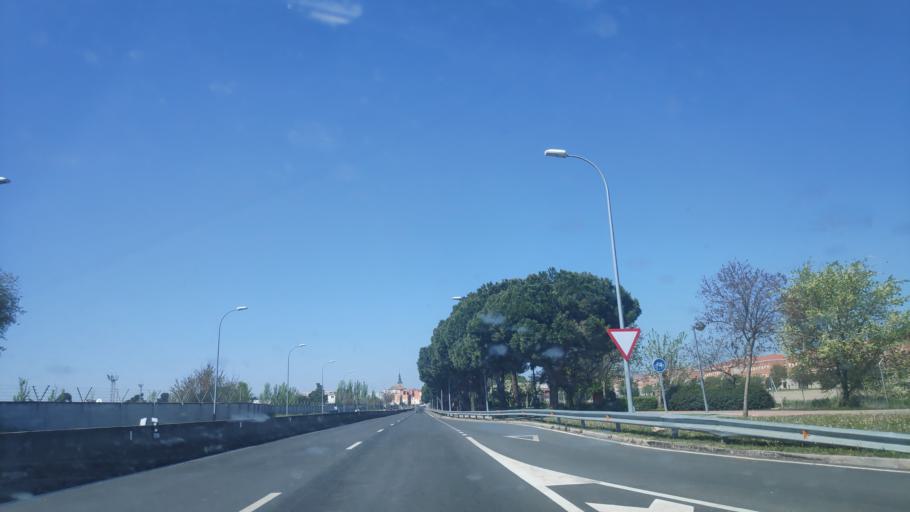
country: ES
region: Madrid
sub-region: Provincia de Madrid
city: Getafe
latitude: 40.3048
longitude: -3.7173
